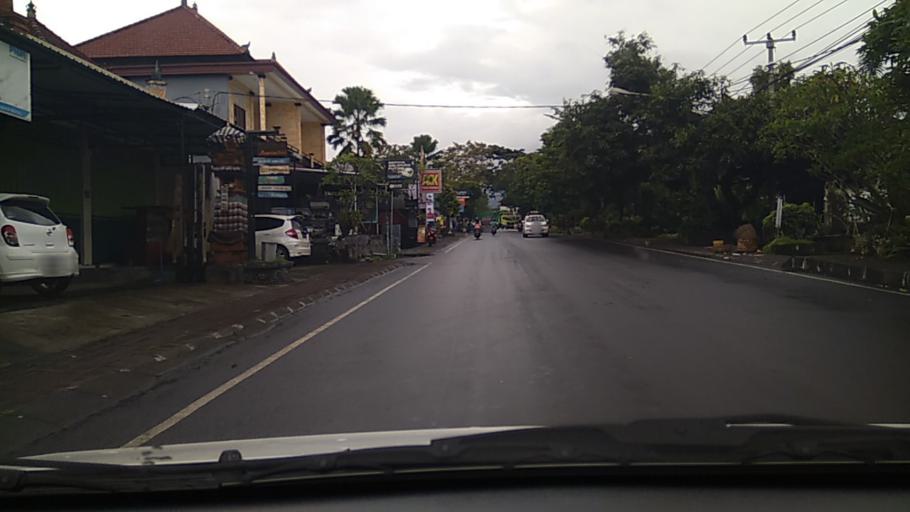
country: ID
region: Bali
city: Subagan
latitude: -8.4406
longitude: 115.5974
